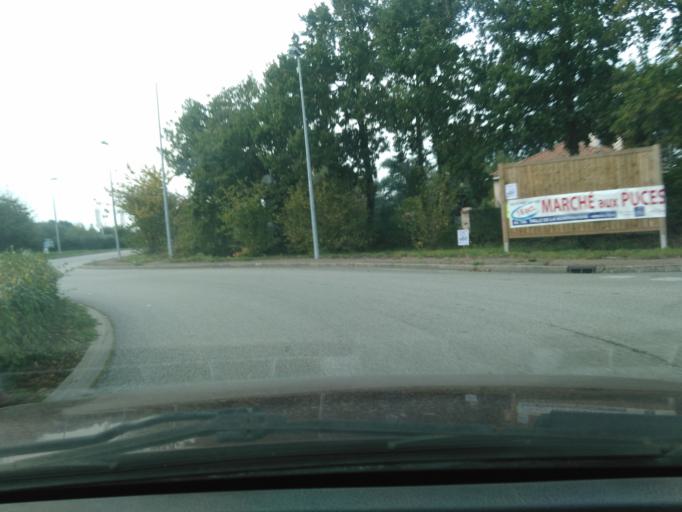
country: FR
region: Pays de la Loire
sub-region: Departement de la Vendee
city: Mouilleron-le-Captif
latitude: 46.7272
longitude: -1.4293
